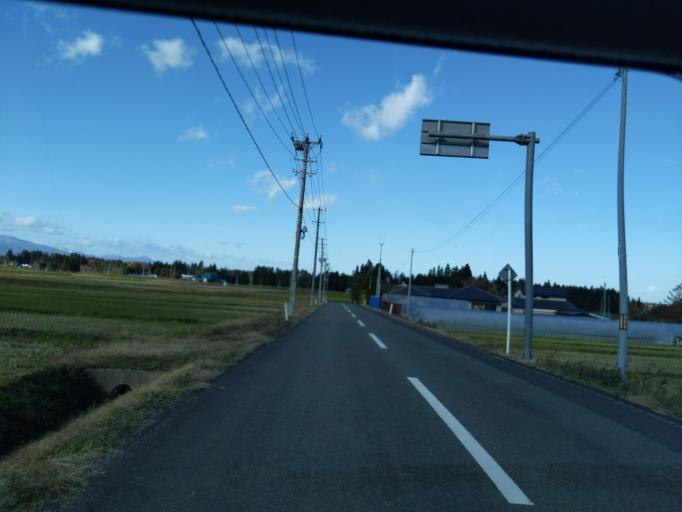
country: JP
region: Iwate
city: Mizusawa
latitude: 39.0666
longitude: 141.1122
